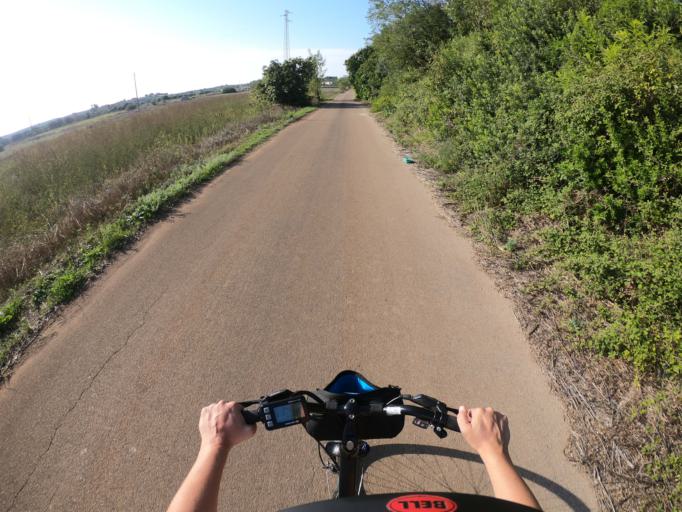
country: IT
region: Apulia
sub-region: Provincia di Lecce
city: Leuca
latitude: 39.8126
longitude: 18.3641
